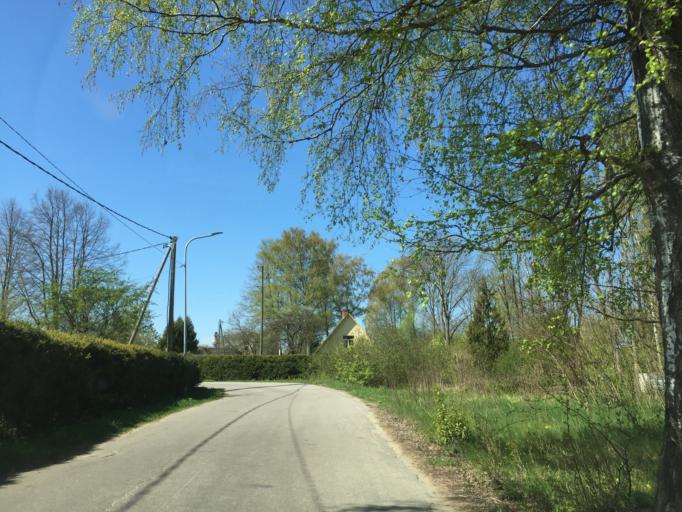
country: LV
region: Saulkrastu
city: Saulkrasti
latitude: 57.3178
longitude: 24.4245
